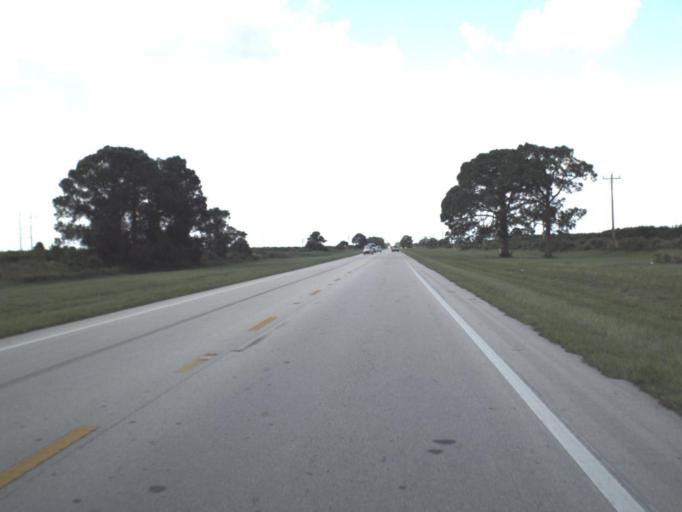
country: US
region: Florida
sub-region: Collier County
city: Immokalee
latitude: 26.4955
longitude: -81.4736
